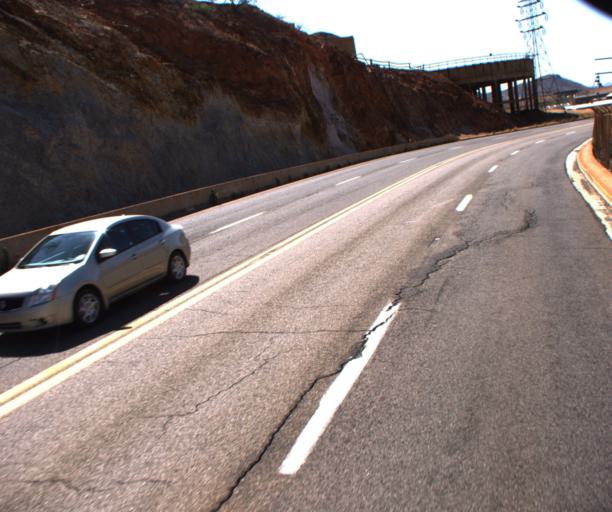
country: US
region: Arizona
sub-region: Cochise County
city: Bisbee
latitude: 31.4343
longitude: -109.8958
